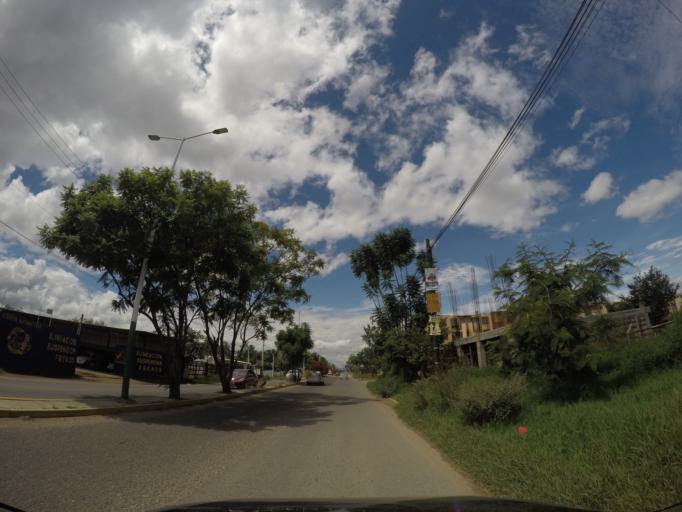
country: MX
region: Oaxaca
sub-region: Santa Cruz Xoxocotlan
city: Santa Cruz Xoxocotlan
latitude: 17.0152
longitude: -96.7336
